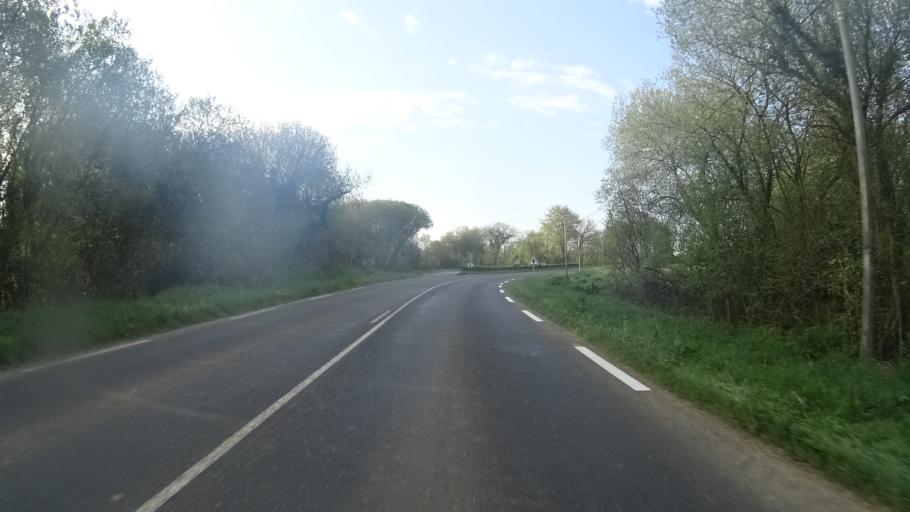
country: FR
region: Brittany
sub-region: Departement du Finistere
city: La Roche-Maurice
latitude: 48.4493
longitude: -4.1827
